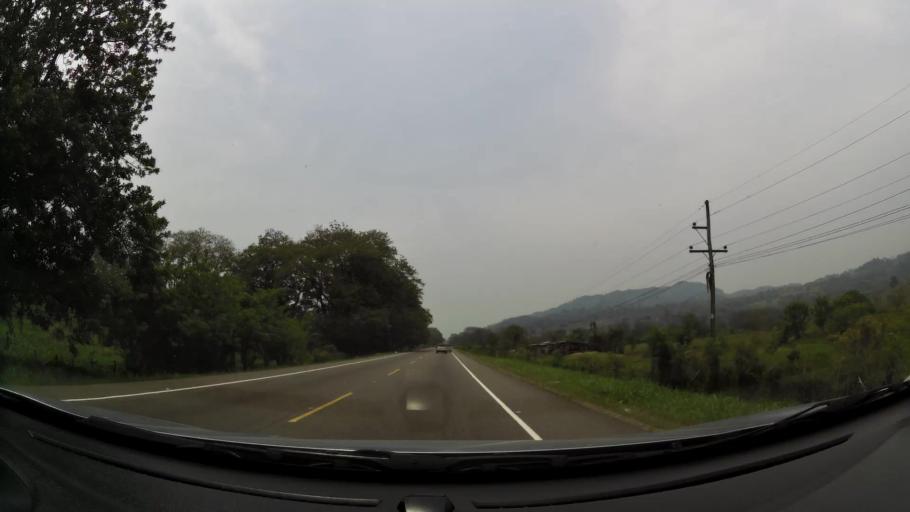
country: HN
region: Cortes
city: La Guama
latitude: 14.8205
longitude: -87.9619
